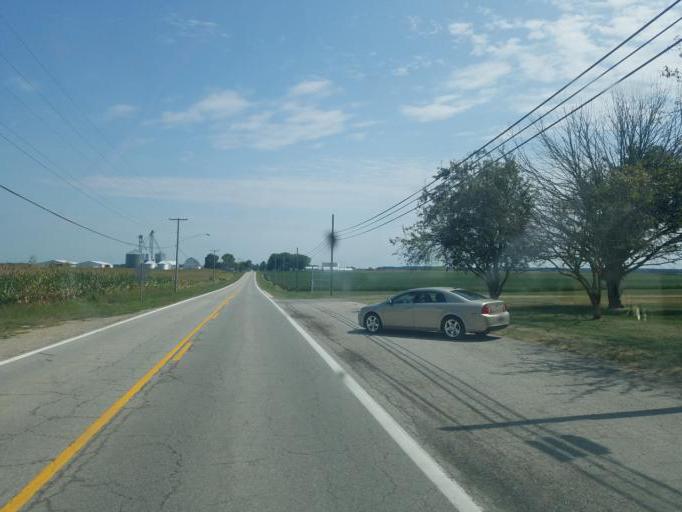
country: US
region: Ohio
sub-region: Marion County
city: Marion
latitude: 40.6878
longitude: -83.2104
